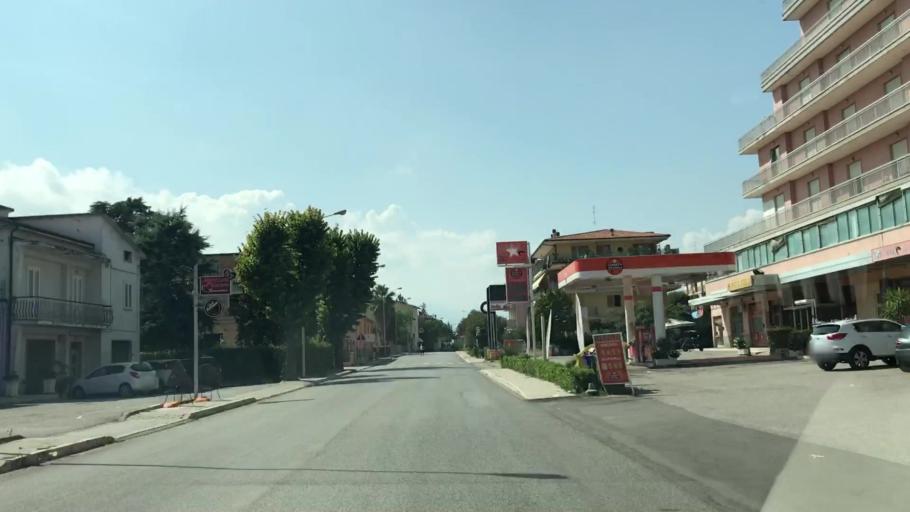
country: IT
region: The Marches
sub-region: Provincia di Ascoli Piceno
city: Stella
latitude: 42.8868
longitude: 13.8088
